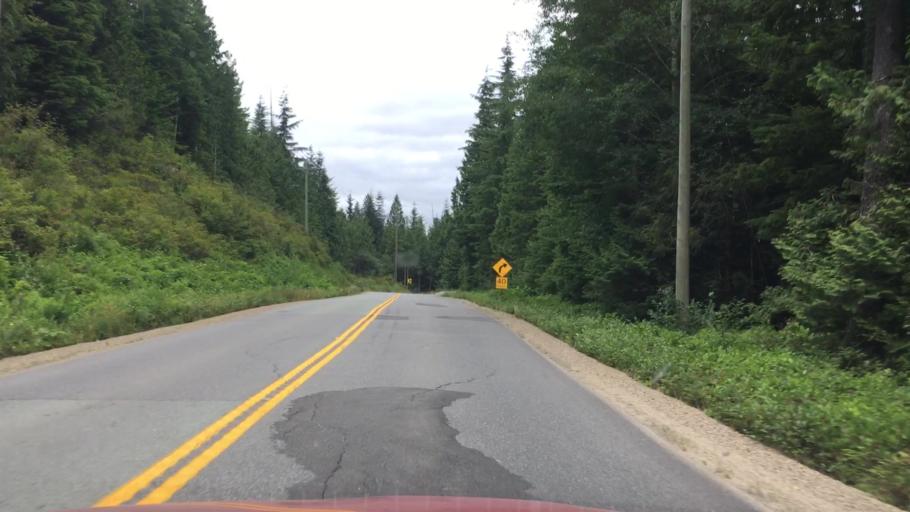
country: CA
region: British Columbia
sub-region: Regional District of Alberni-Clayoquot
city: Ucluelet
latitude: 49.0338
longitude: -125.5401
